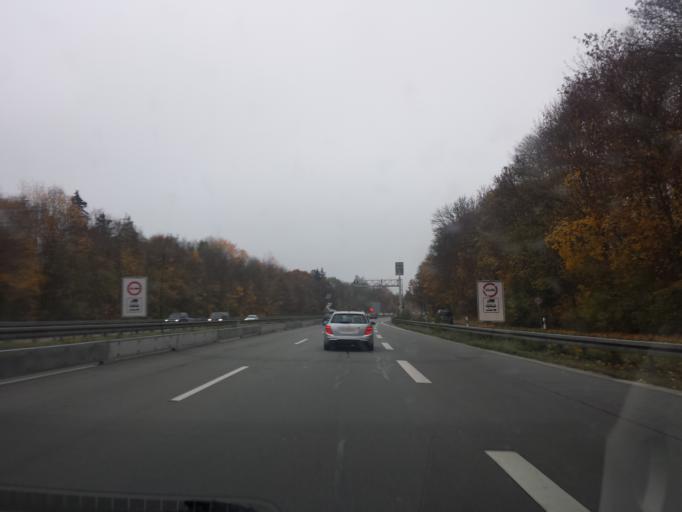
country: DE
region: Bavaria
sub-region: Upper Bavaria
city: Neuried
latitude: 48.0803
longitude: 11.4878
